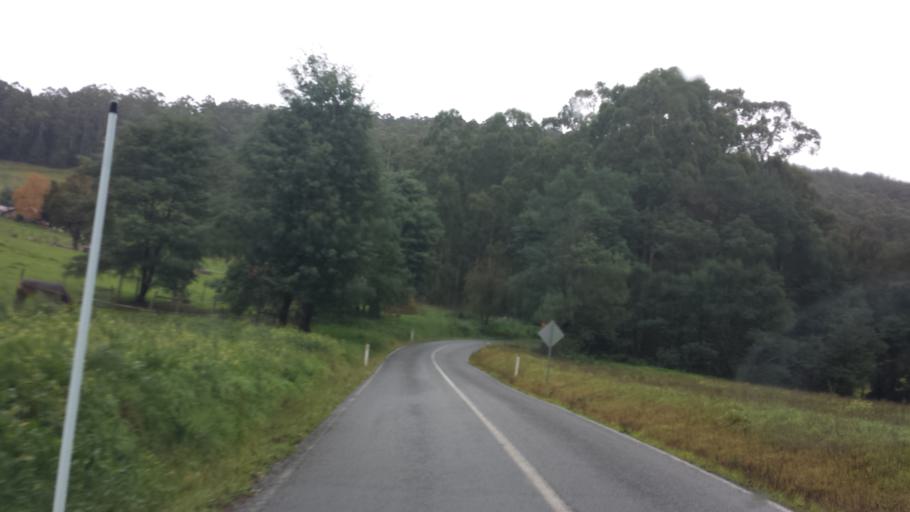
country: AU
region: Victoria
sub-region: Yarra Ranges
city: Monbulk
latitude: -37.8996
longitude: 145.4139
